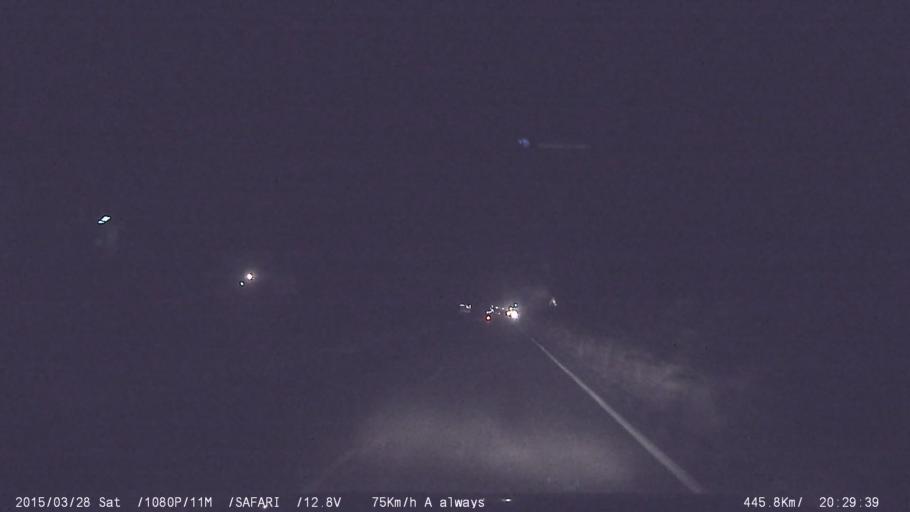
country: IN
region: Karnataka
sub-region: Mandya
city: Maddur
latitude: 12.6132
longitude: 77.0686
